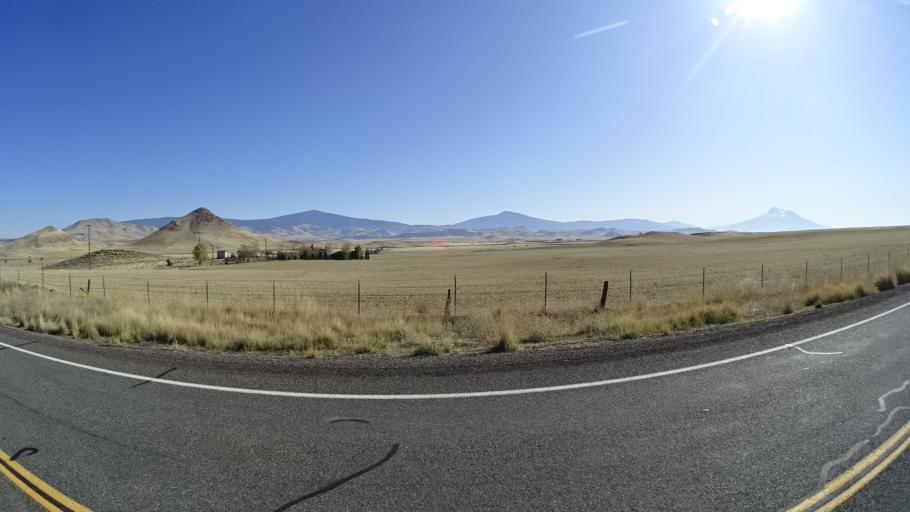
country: US
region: California
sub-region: Siskiyou County
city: Montague
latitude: 41.8150
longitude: -122.4978
